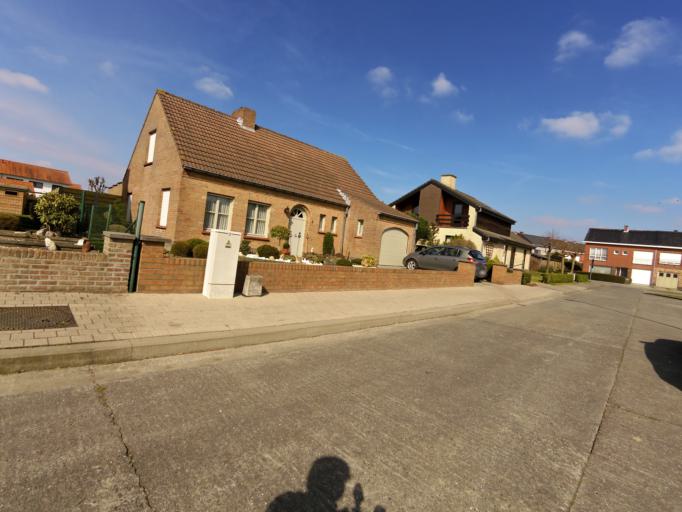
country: BE
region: Flanders
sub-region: Provincie West-Vlaanderen
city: Torhout
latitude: 51.0671
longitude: 3.0806
